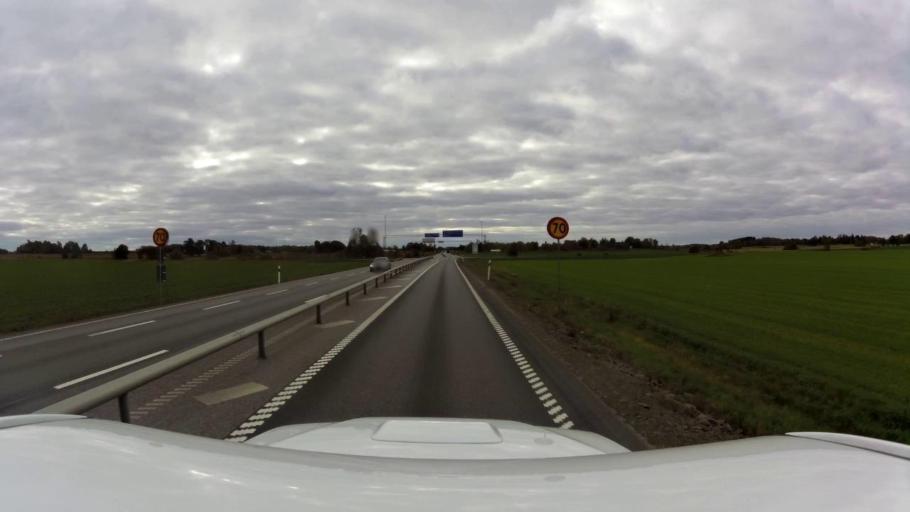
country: SE
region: OEstergoetland
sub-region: Linkopings Kommun
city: Malmslatt
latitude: 58.3524
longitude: 15.5482
